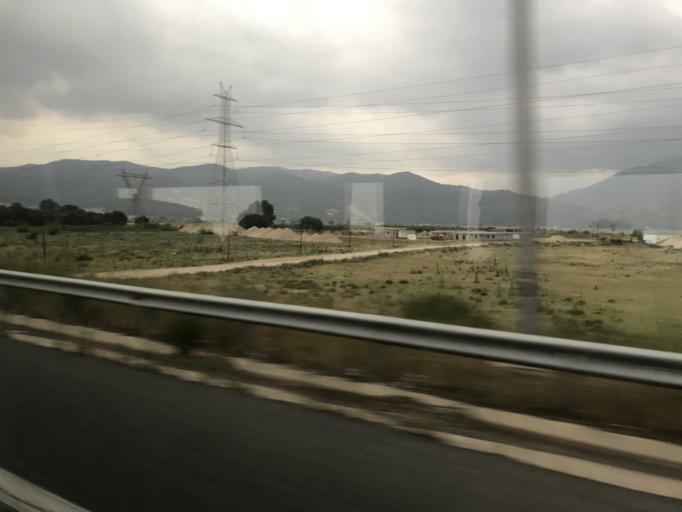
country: GR
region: East Macedonia and Thrace
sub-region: Nomos Rodopis
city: Iasmos
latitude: 41.1134
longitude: 25.2069
